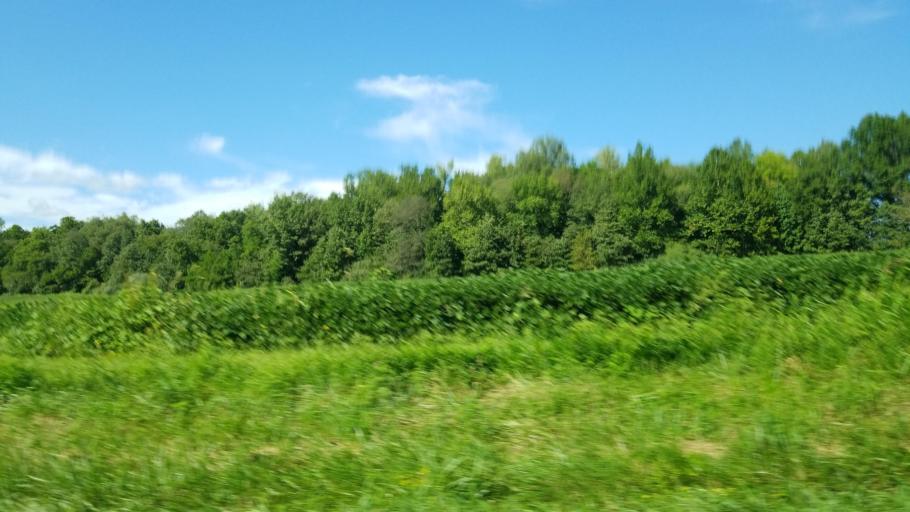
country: US
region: Illinois
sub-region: Williamson County
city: Marion
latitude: 37.7446
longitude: -88.8842
